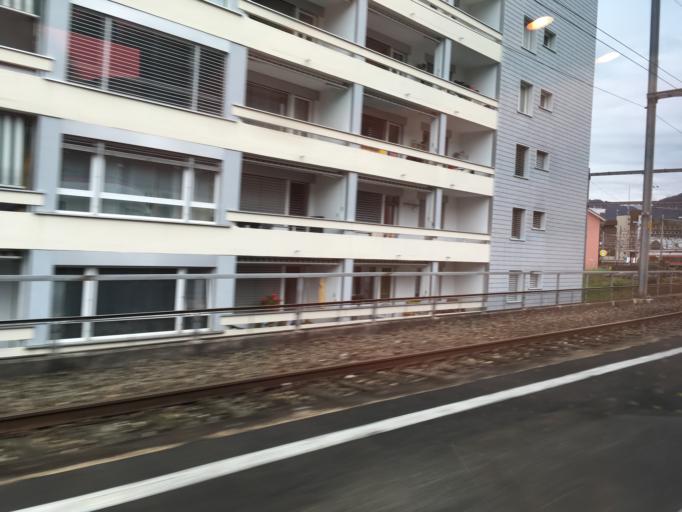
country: CH
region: Schwyz
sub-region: Bezirk Schwyz
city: Goldau
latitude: 47.0505
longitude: 8.5483
